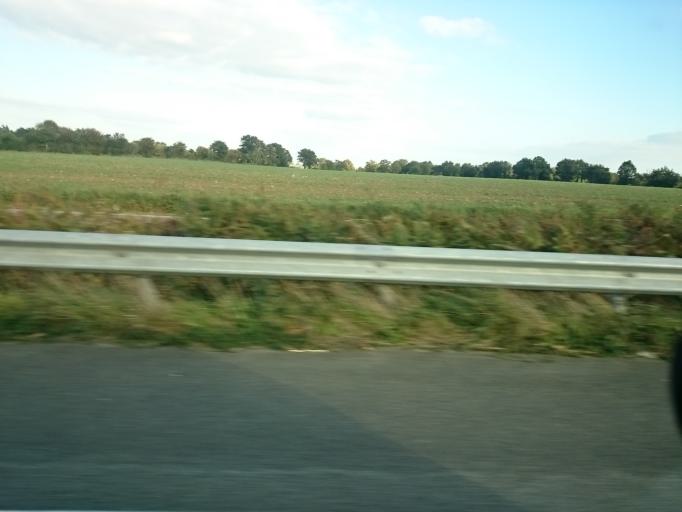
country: FR
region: Pays de la Loire
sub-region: Departement de la Loire-Atlantique
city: Jans
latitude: 47.5986
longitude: -1.6275
